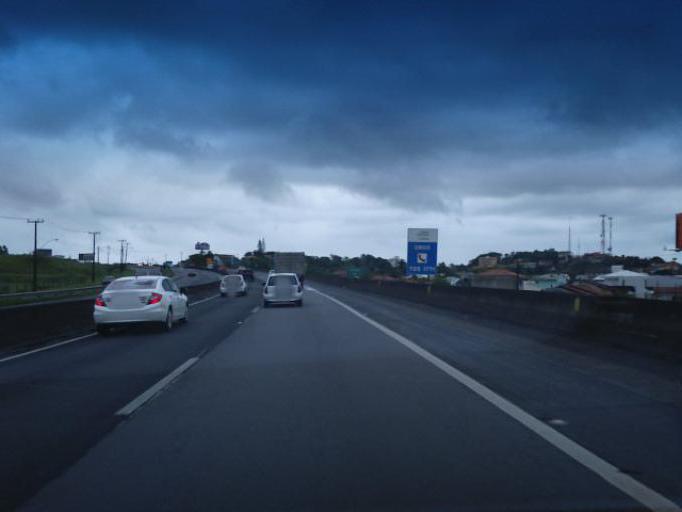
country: BR
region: Santa Catarina
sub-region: Barra Velha
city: Barra Velha
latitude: -26.6437
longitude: -48.6884
